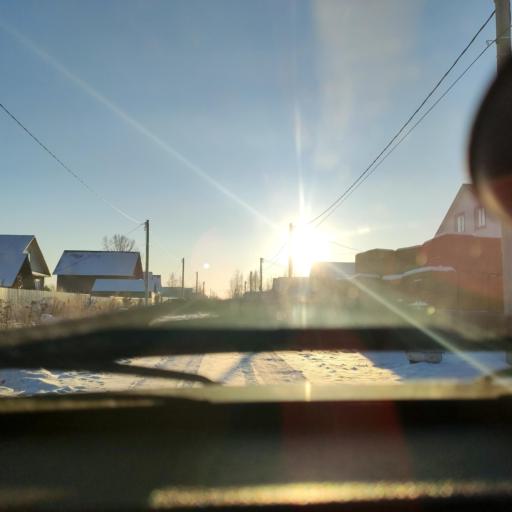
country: RU
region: Bashkortostan
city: Ufa
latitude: 54.8344
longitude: 56.1745
